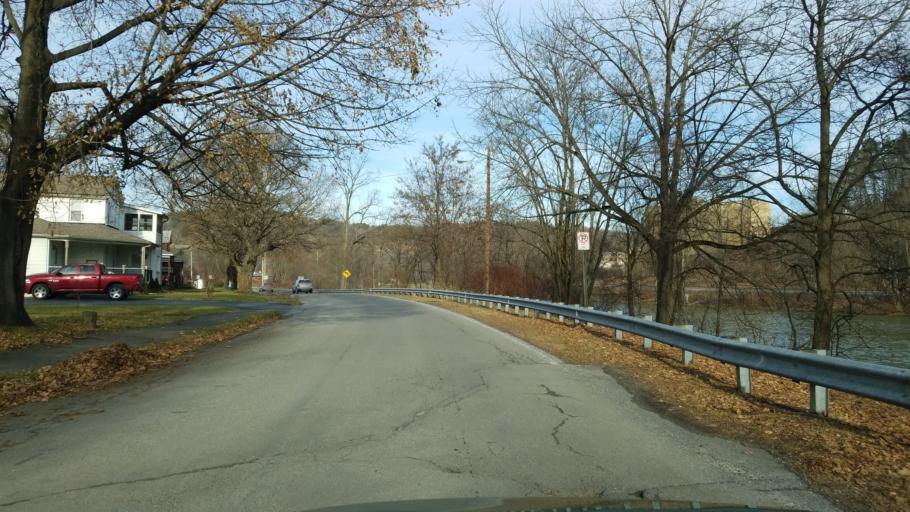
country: US
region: Pennsylvania
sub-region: Clearfield County
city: Clearfield
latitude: 41.0283
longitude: -78.4383
